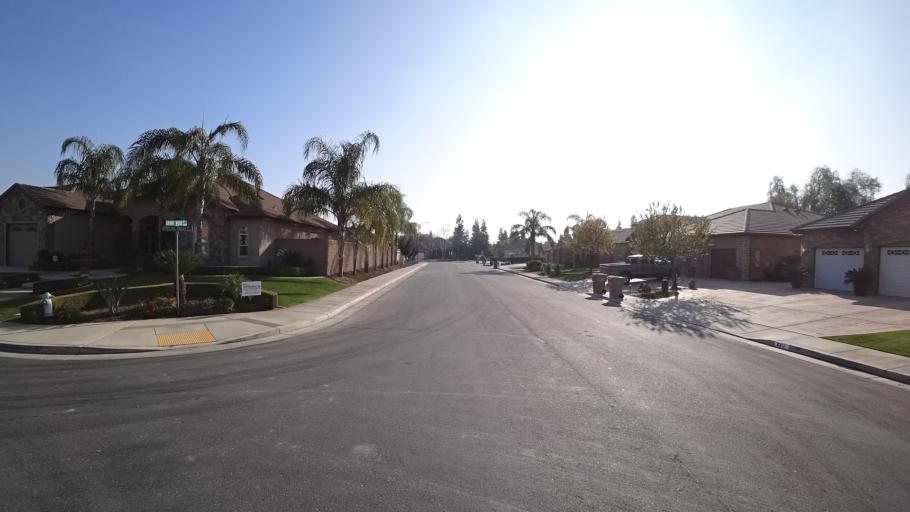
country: US
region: California
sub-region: Kern County
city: Greenacres
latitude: 35.4182
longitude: -119.0975
